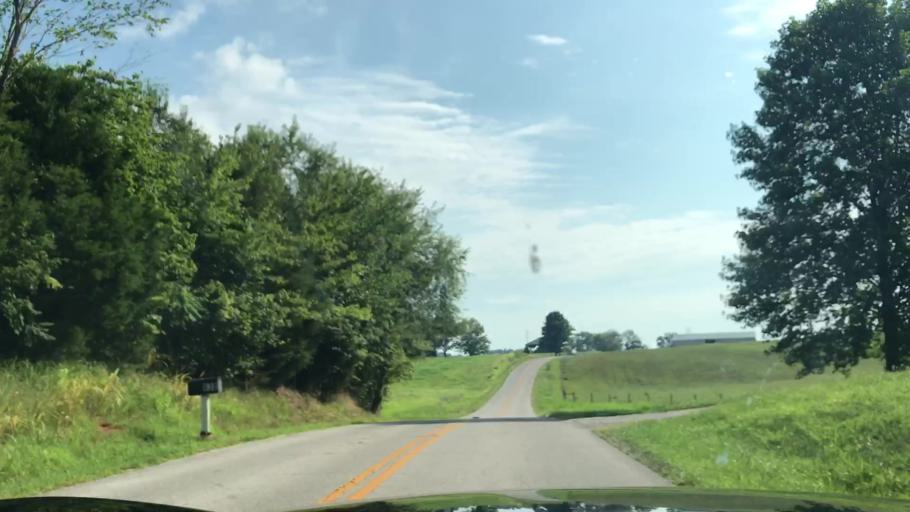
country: US
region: Kentucky
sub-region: Hart County
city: Munfordville
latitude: 37.2254
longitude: -85.7200
